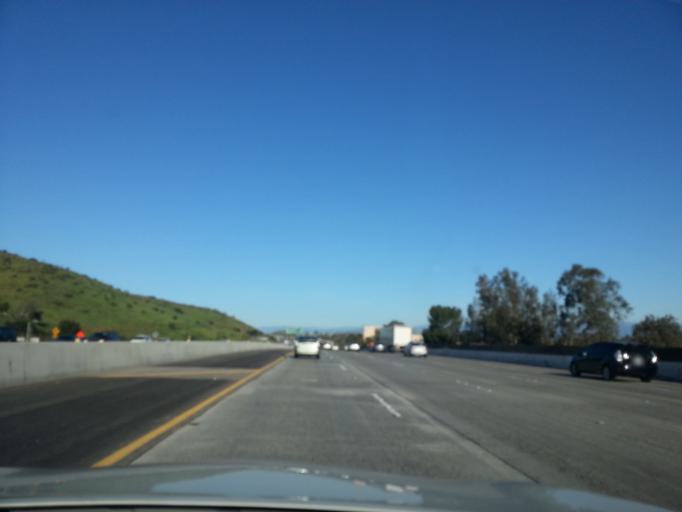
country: US
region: California
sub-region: Ventura County
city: Thousand Oaks
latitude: 34.1705
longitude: -118.8444
